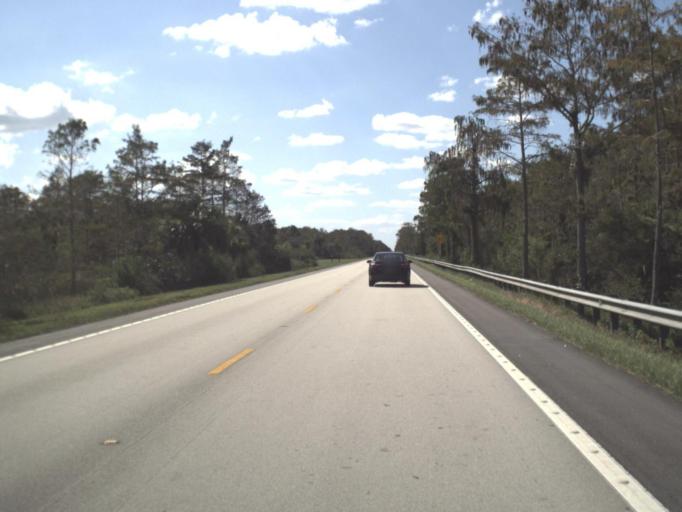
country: US
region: Florida
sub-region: Miami-Dade County
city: Kendall West
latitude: 25.8522
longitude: -80.9872
